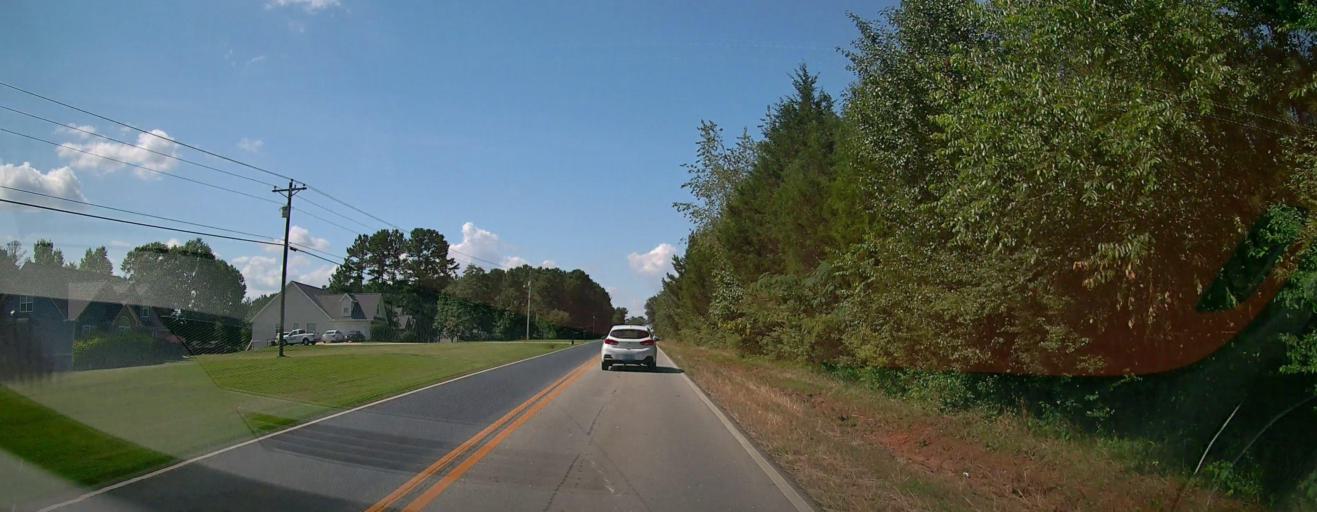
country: US
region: Georgia
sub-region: Spalding County
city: East Griffin
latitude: 33.2875
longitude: -84.1898
